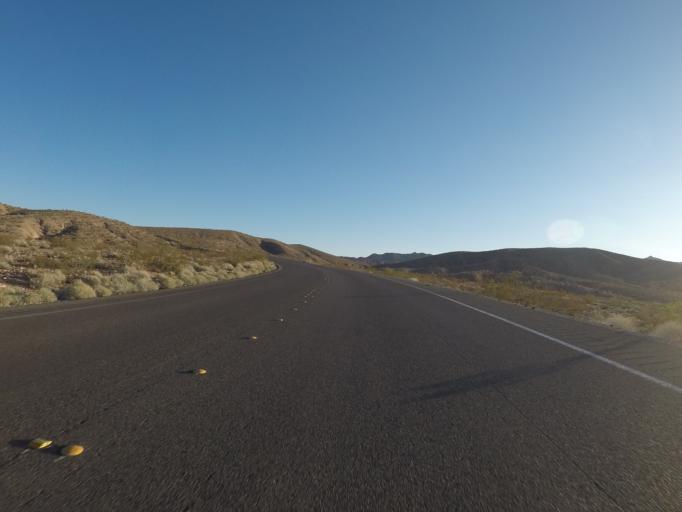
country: US
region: Nevada
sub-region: Clark County
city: Moapa Valley
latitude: 36.2774
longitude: -114.4880
